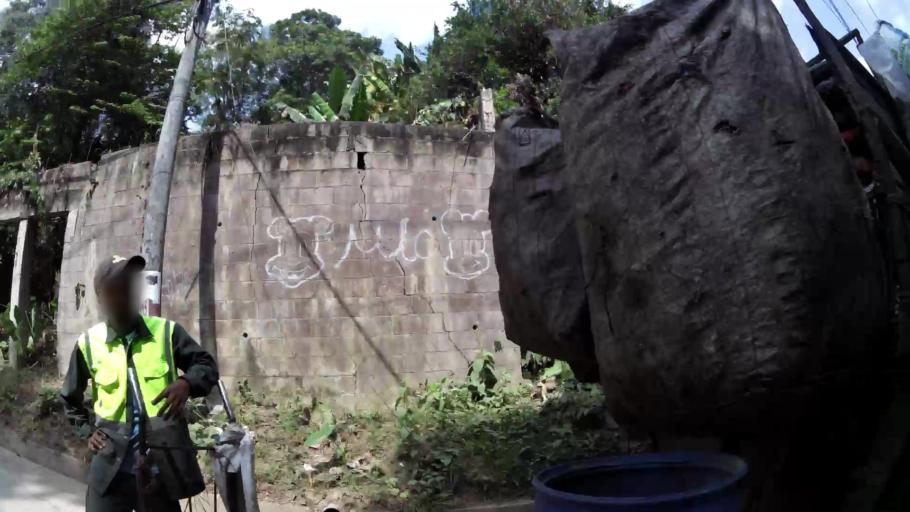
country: SV
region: San Salvador
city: Mejicanos
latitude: 13.7156
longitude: -89.2368
